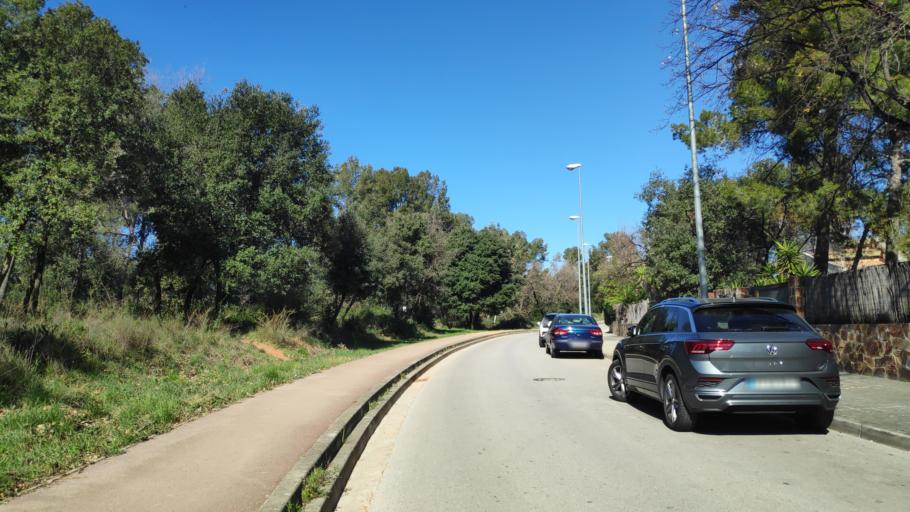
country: ES
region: Catalonia
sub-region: Provincia de Barcelona
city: Sant Quirze del Valles
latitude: 41.5559
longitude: 2.0702
